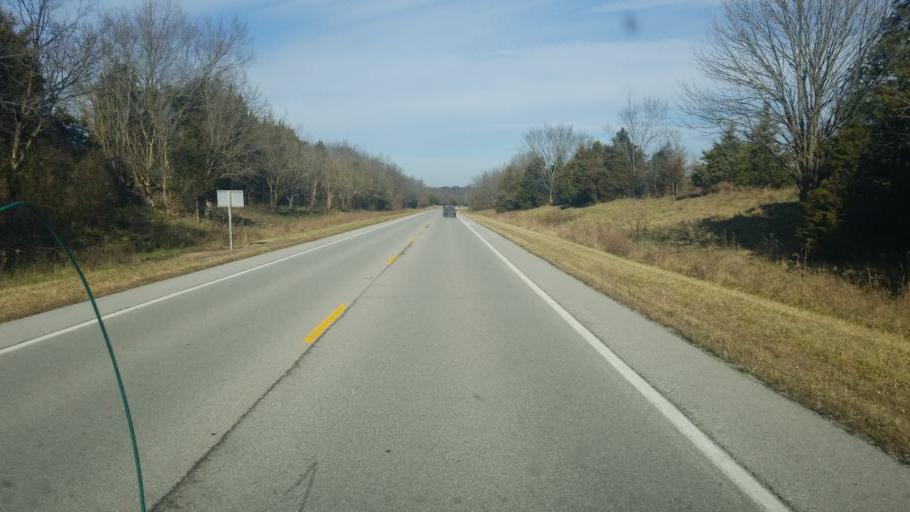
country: US
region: Illinois
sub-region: Union County
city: Cobden
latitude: 37.6240
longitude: -89.2351
